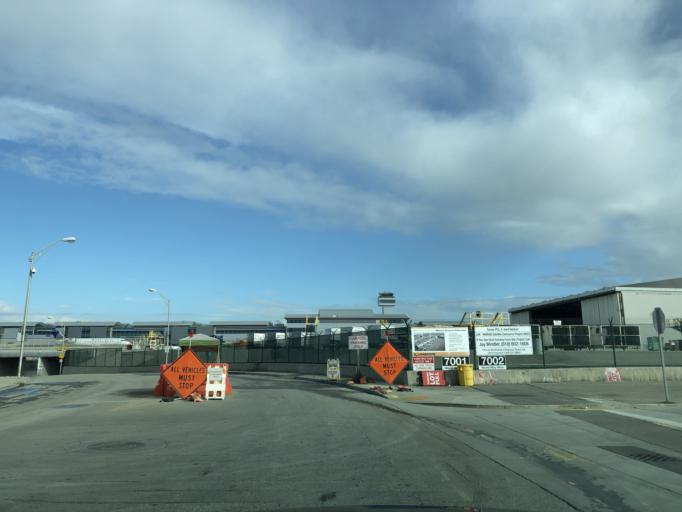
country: US
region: California
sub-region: Los Angeles County
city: El Segundo
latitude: 33.9421
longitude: -118.4197
